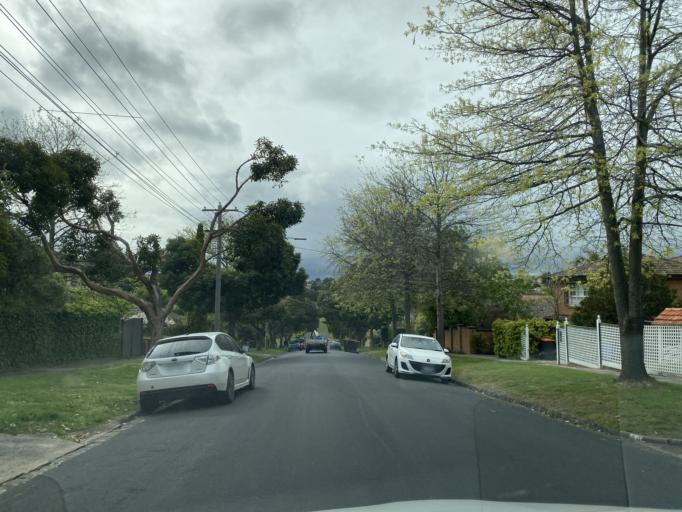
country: AU
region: Victoria
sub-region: Boroondara
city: Camberwell
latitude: -37.8432
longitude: 145.0816
